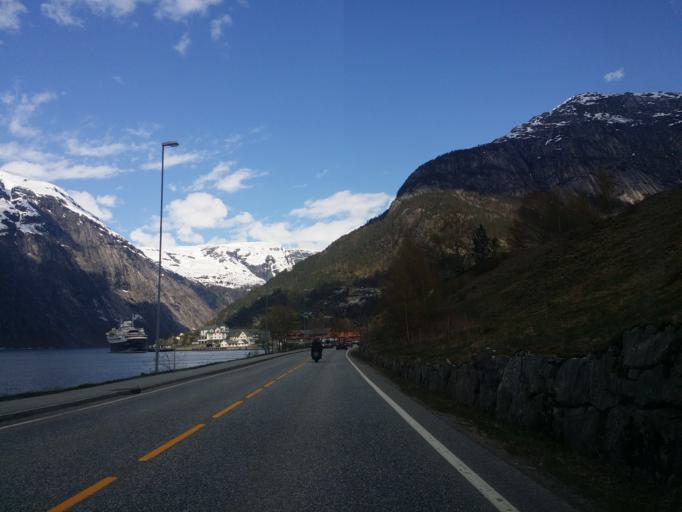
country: NO
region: Hordaland
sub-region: Eidfjord
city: Eidfjord
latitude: 60.4640
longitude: 7.0610
